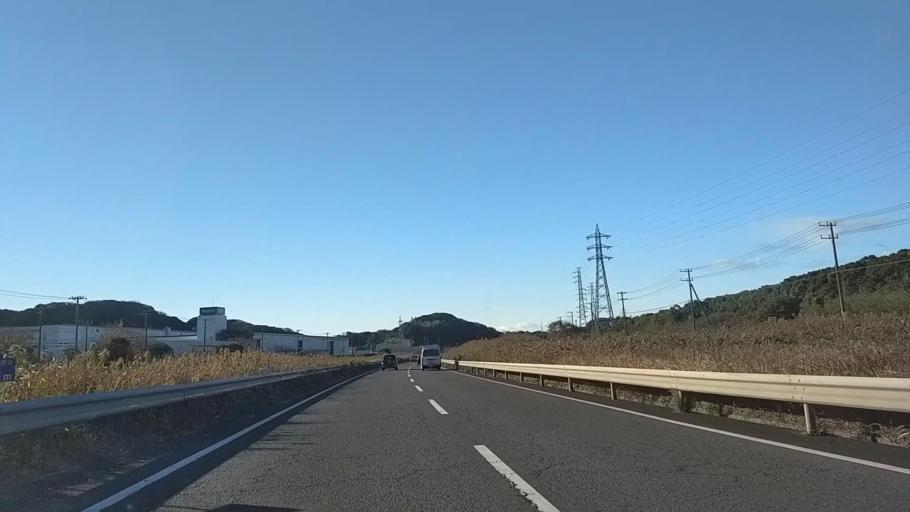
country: JP
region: Chiba
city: Kisarazu
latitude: 35.3612
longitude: 139.9110
